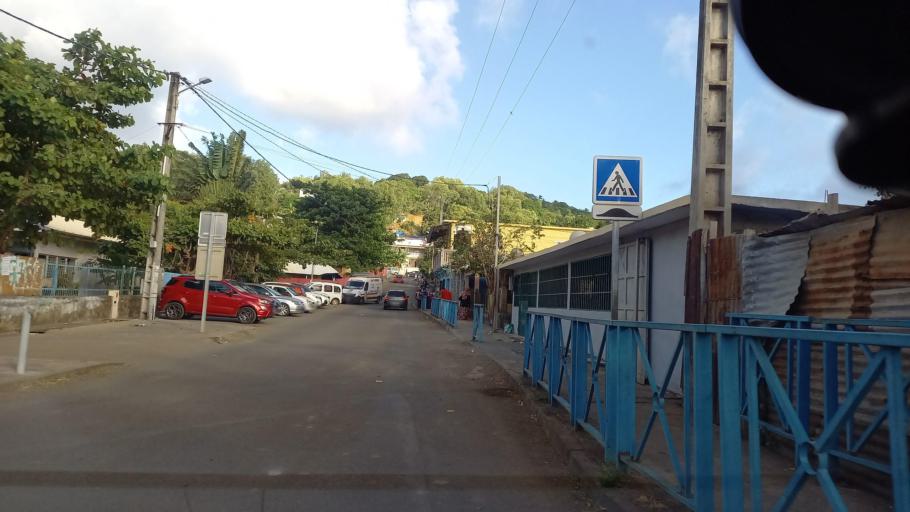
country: YT
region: Bandrele
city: Bandrele
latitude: -12.9144
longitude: 45.1939
